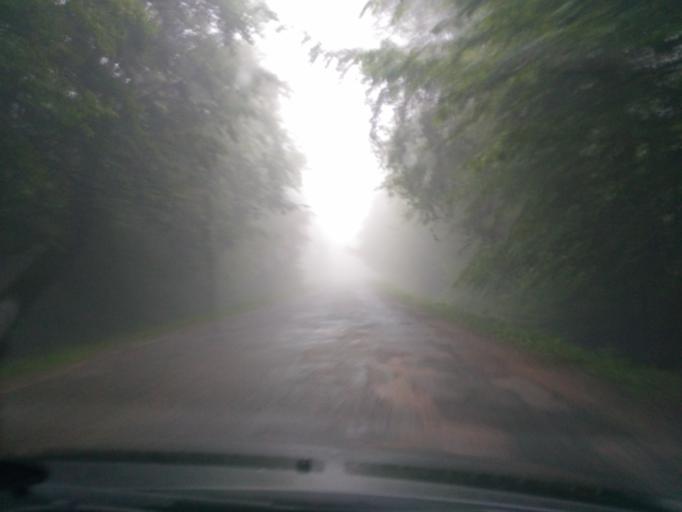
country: PL
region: Subcarpathian Voivodeship
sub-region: Powiat debicki
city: Debica
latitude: 49.9694
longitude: 21.4235
